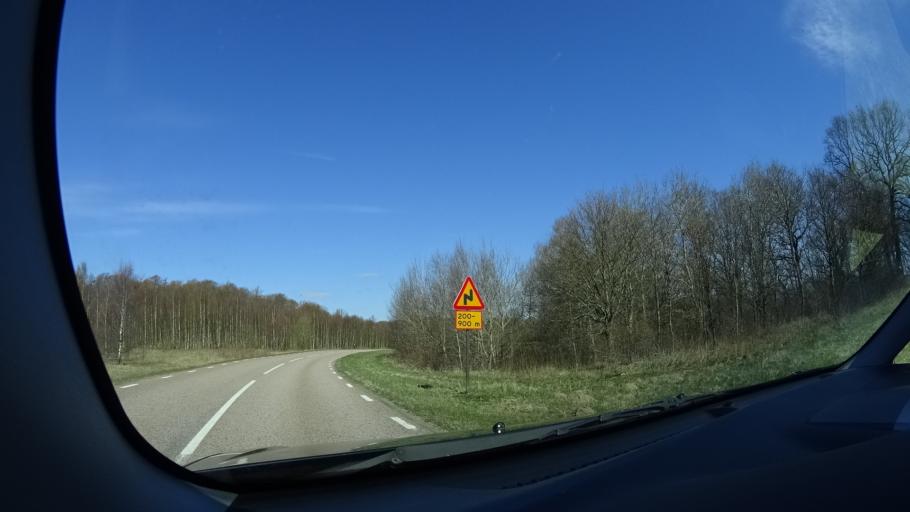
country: SE
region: Skane
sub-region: Astorps Kommun
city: Kvidinge
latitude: 56.1071
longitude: 13.0962
